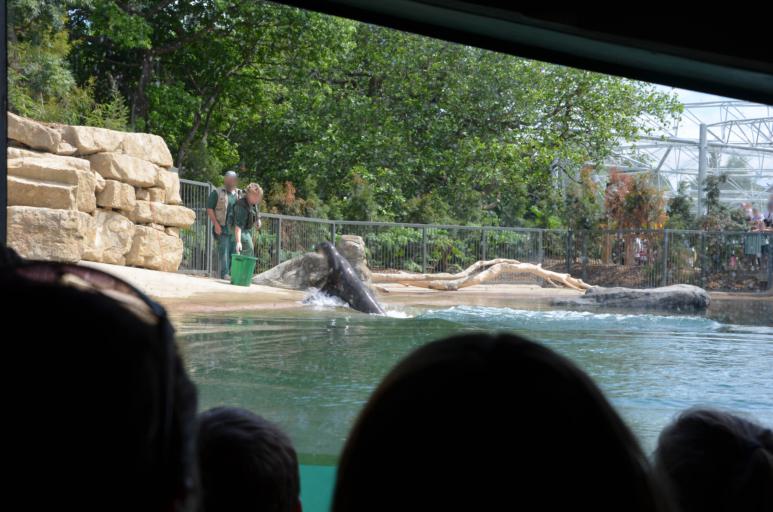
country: IE
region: Leinster
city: Cabra
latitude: 53.3560
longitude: -6.3060
